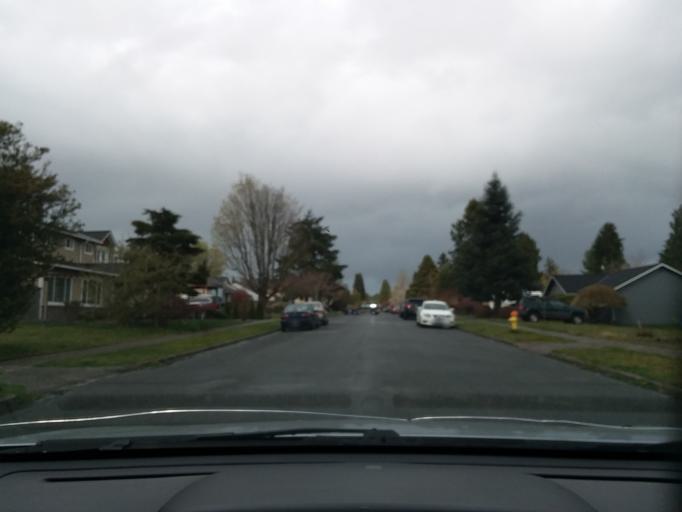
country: US
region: Washington
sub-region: King County
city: Shoreline
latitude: 47.7417
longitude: -122.3196
